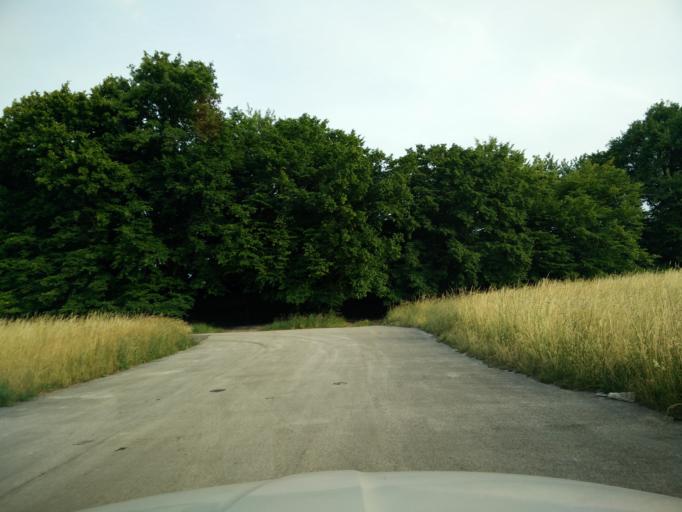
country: SK
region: Nitriansky
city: Prievidza
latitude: 48.7711
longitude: 18.6553
